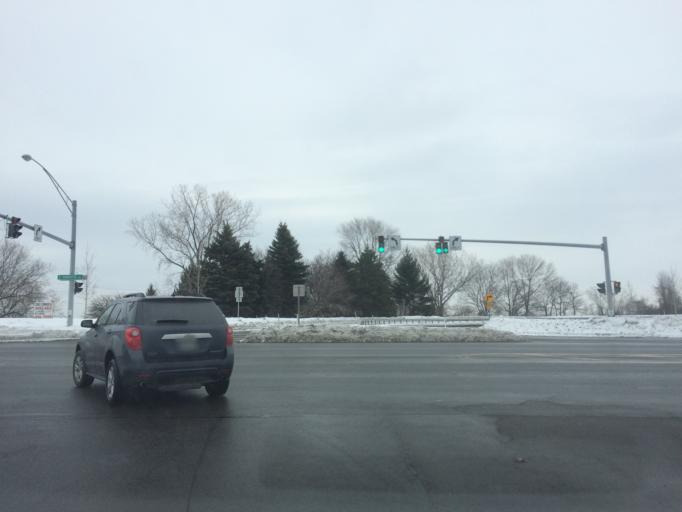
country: US
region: New York
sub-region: Monroe County
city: Rochester
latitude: 43.0959
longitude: -77.6125
